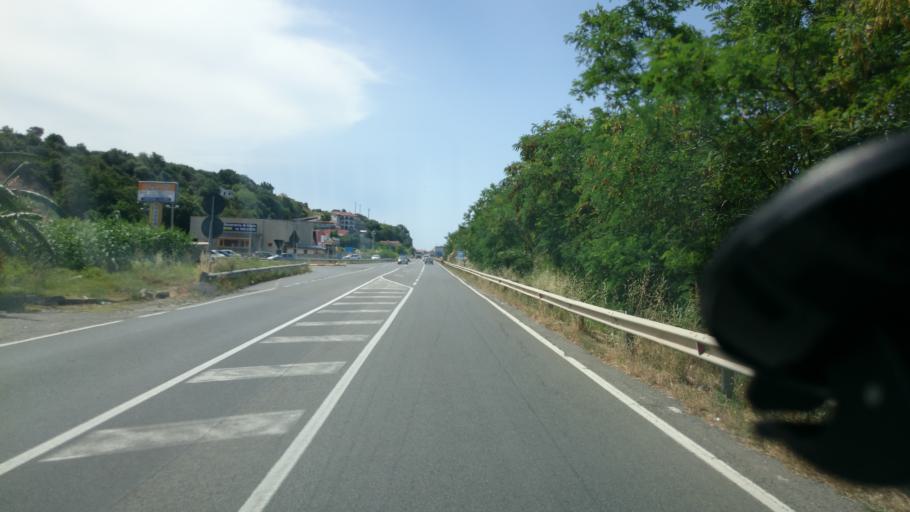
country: IT
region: Calabria
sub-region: Provincia di Cosenza
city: Diamante
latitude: 39.6856
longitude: 15.8193
